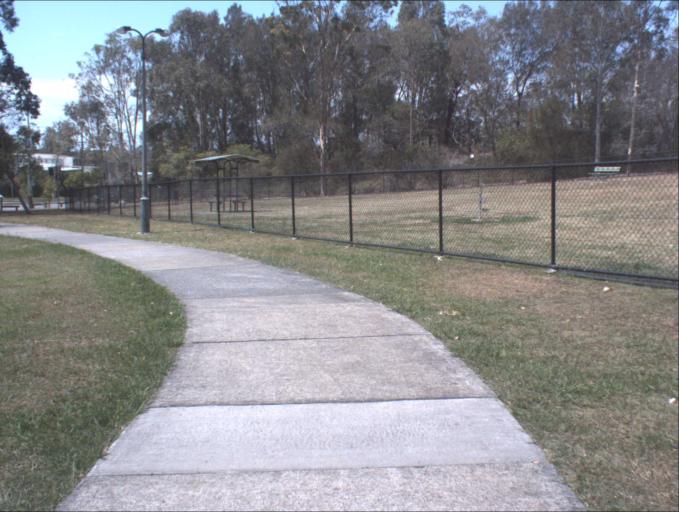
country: AU
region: Queensland
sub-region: Logan
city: Rochedale South
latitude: -27.6066
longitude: 153.1072
